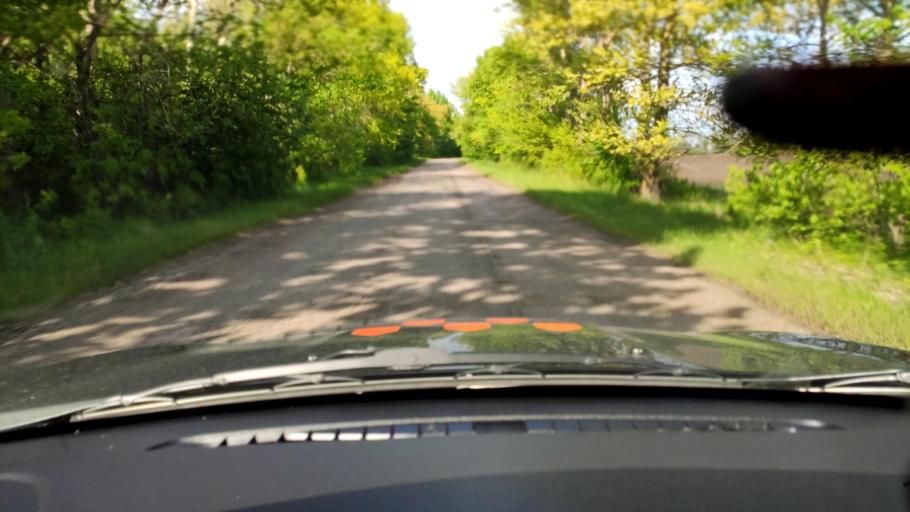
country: RU
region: Voronezj
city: Uryv-Pokrovka
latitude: 51.2041
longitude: 39.0699
